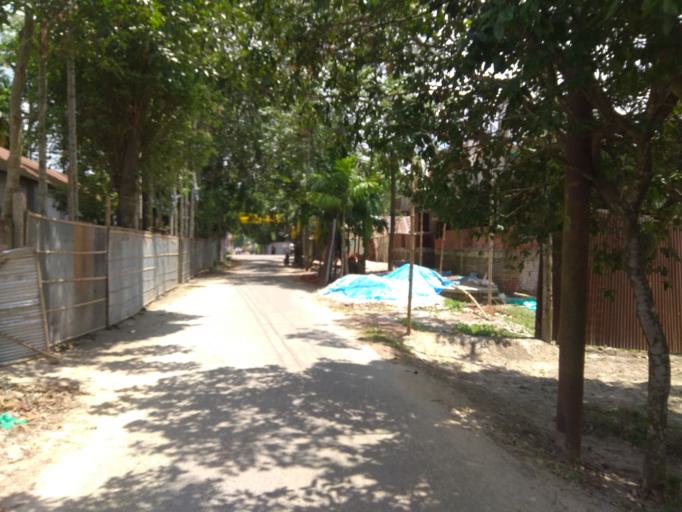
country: IN
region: West Bengal
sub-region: Koch Bihar
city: Haldibari
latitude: 26.1519
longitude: 88.9261
